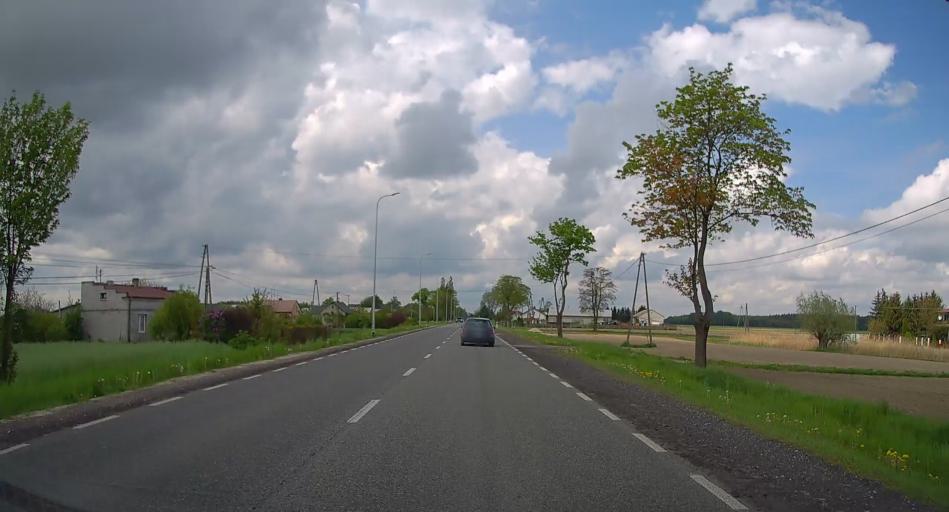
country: PL
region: Masovian Voivodeship
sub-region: Powiat plonski
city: Zaluski
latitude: 52.4447
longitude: 20.5206
